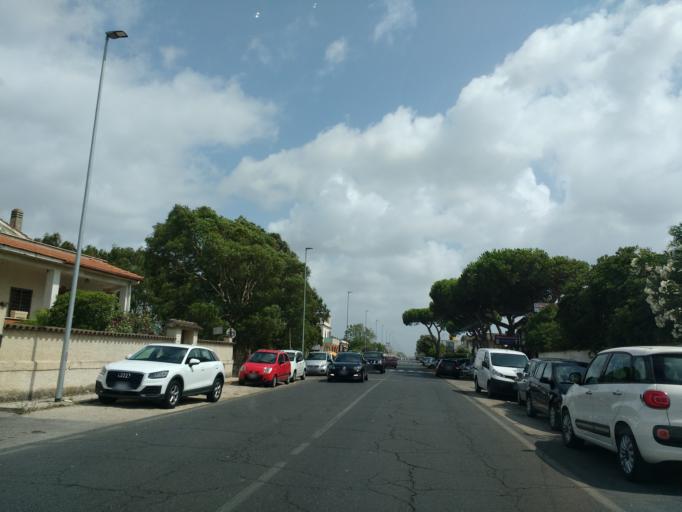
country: IT
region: Latium
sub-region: Citta metropolitana di Roma Capitale
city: Marina di Ardea-Tor San Lorenzo
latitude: 41.5668
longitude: 12.5246
